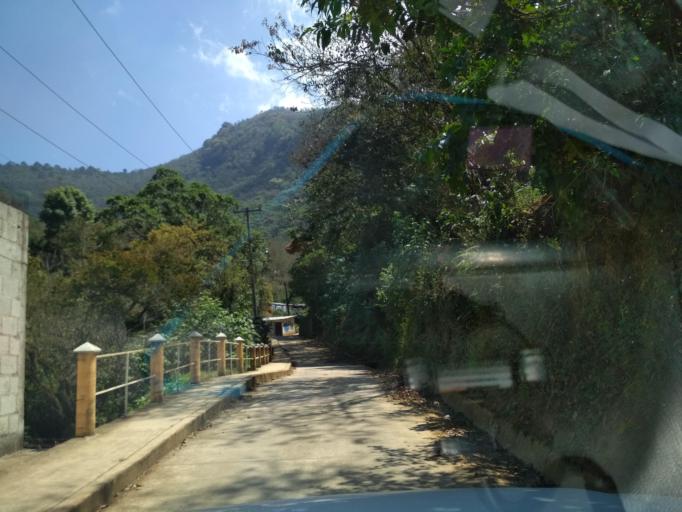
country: MX
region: Veracruz
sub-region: Tlilapan
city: Tonalixco
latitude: 18.7767
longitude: -97.0763
